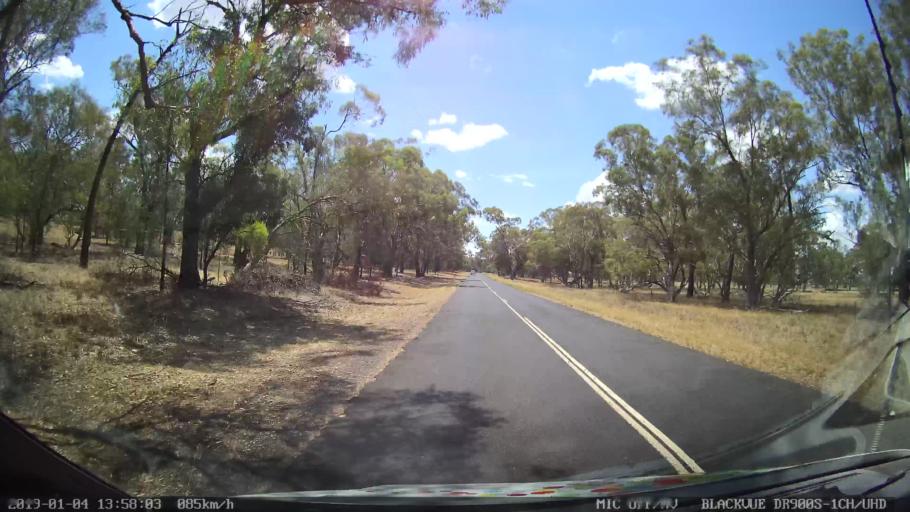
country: AU
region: New South Wales
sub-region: Dubbo Municipality
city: Dubbo
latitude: -32.3332
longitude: 148.5953
